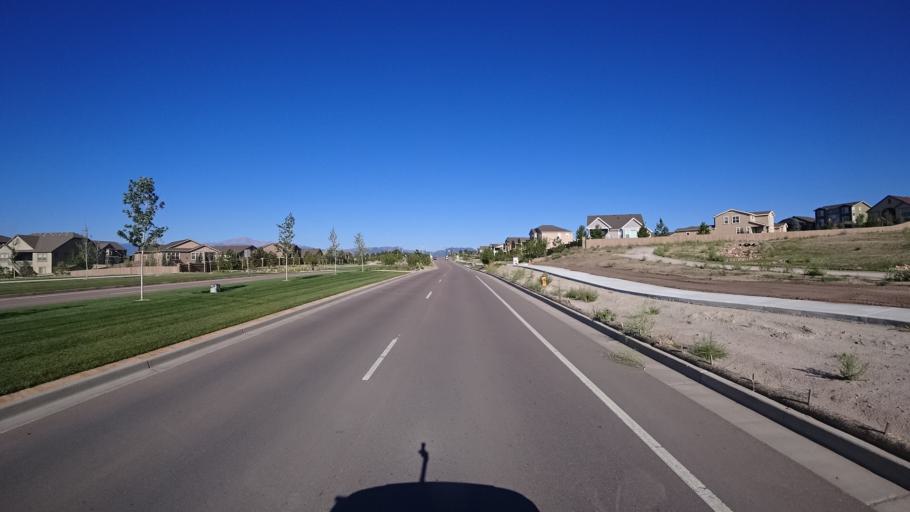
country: US
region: Colorado
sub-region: El Paso County
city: Black Forest
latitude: 38.9711
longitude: -104.7283
